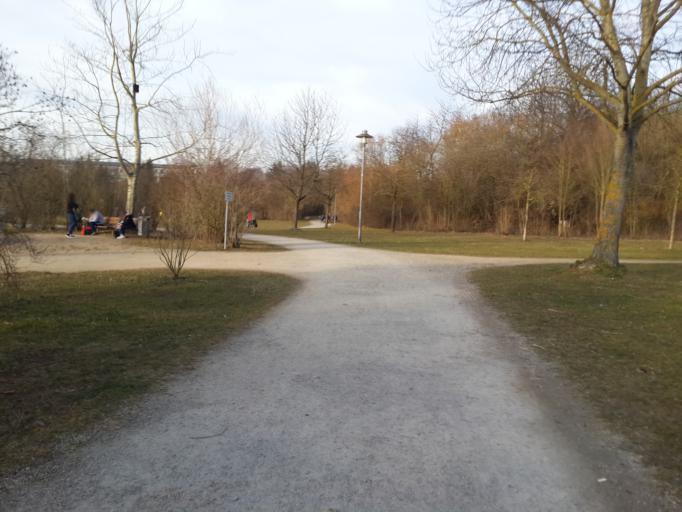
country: DE
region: Baden-Wuerttemberg
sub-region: Regierungsbezirk Stuttgart
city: Heilbronn
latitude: 49.1336
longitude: 9.1815
